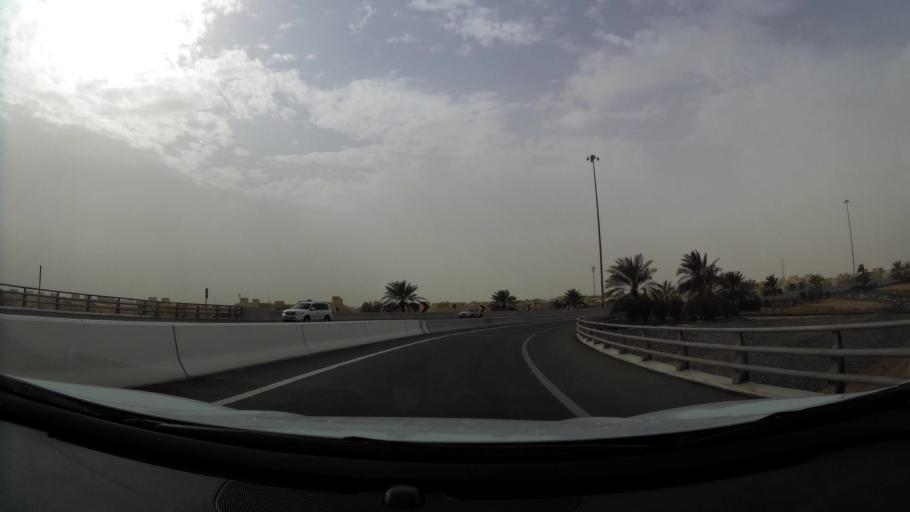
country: AE
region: Abu Dhabi
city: Abu Dhabi
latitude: 24.4398
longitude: 54.5863
